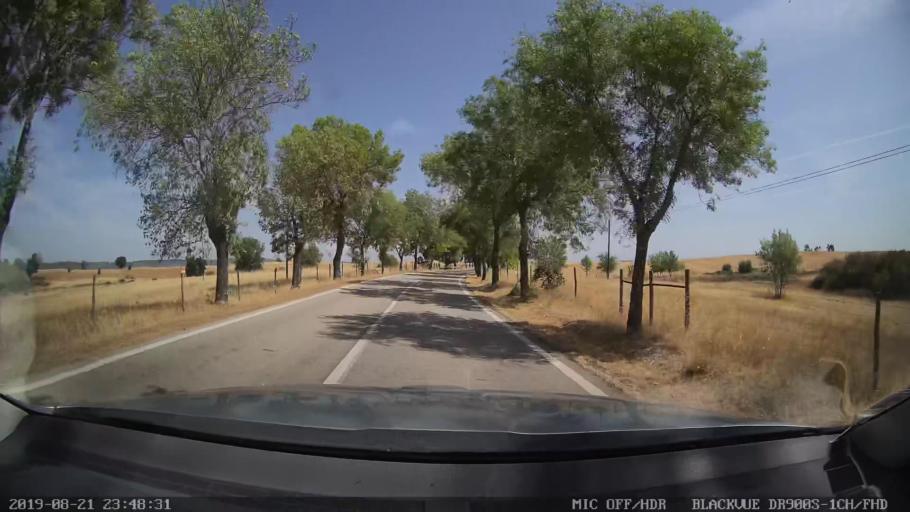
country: PT
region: Castelo Branco
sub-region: Idanha-A-Nova
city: Idanha-a-Nova
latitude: 39.8665
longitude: -7.2568
